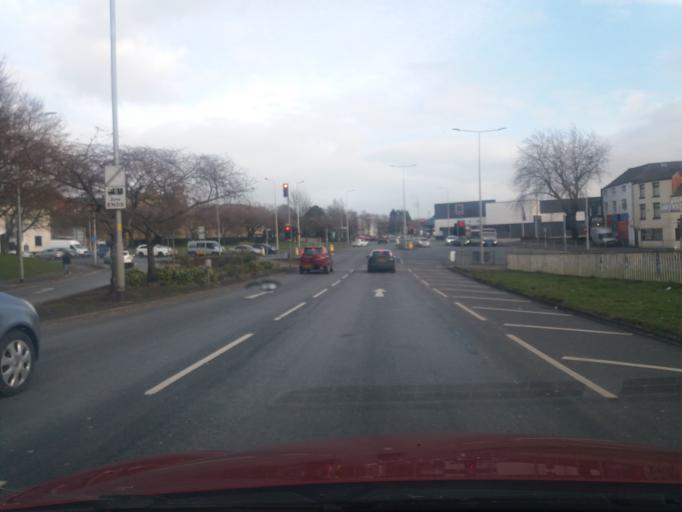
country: GB
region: England
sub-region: Lancashire
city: Preston
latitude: 53.7615
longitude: -2.6915
